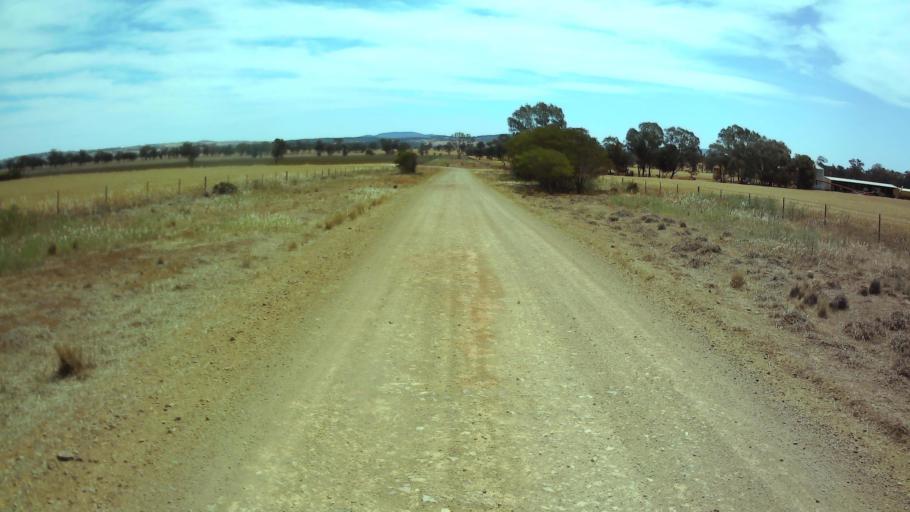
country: AU
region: New South Wales
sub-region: Weddin
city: Grenfell
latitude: -33.7494
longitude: 148.1479
